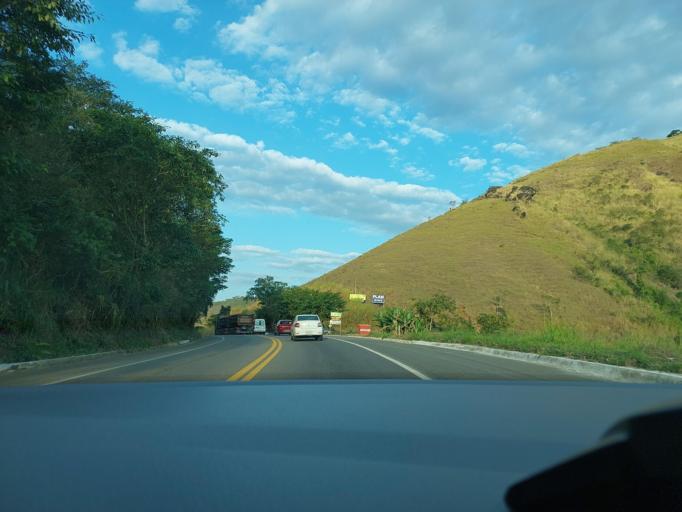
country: BR
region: Minas Gerais
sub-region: Muriae
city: Muriae
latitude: -21.1259
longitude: -42.2511
